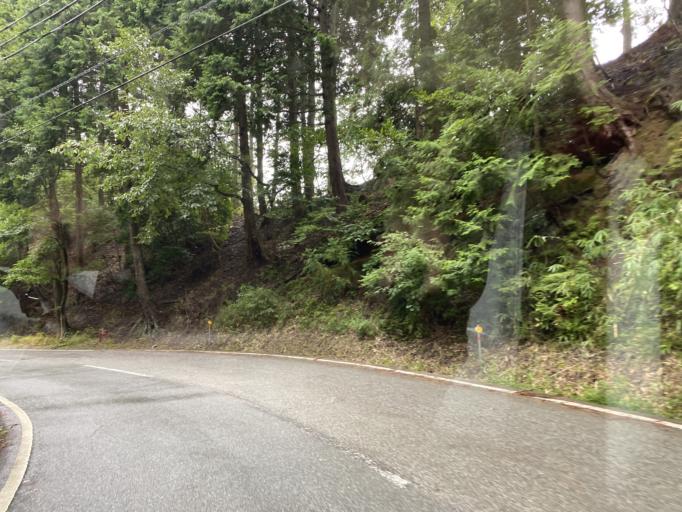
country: JP
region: Kyoto
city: Fukuchiyama
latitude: 35.3043
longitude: 134.9340
